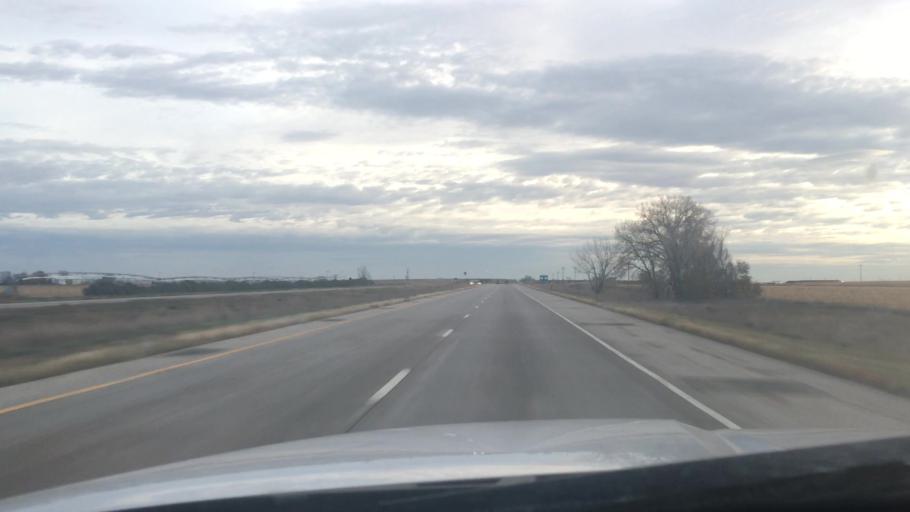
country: US
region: Colorado
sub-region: Morgan County
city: Fort Morgan
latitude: 40.2403
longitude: -104.0705
